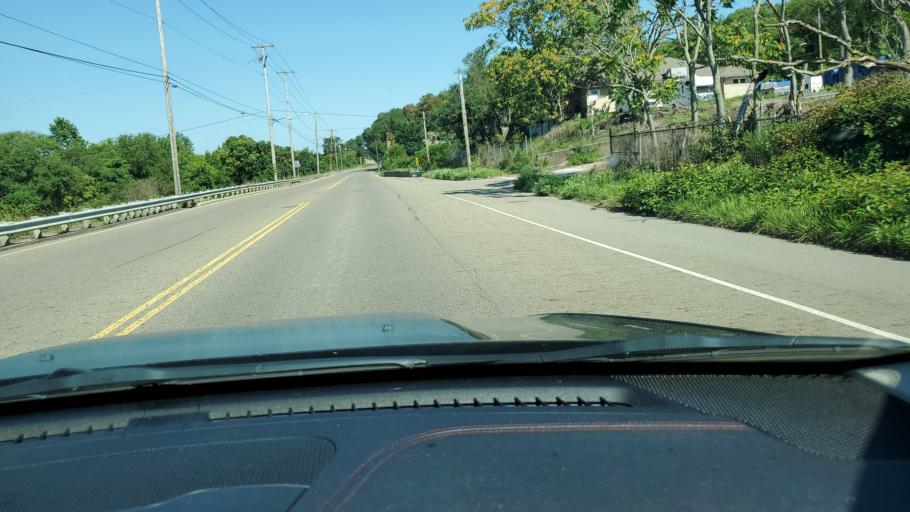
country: US
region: Ohio
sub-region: Mahoning County
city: Campbell
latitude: 41.0683
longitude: -80.5950
